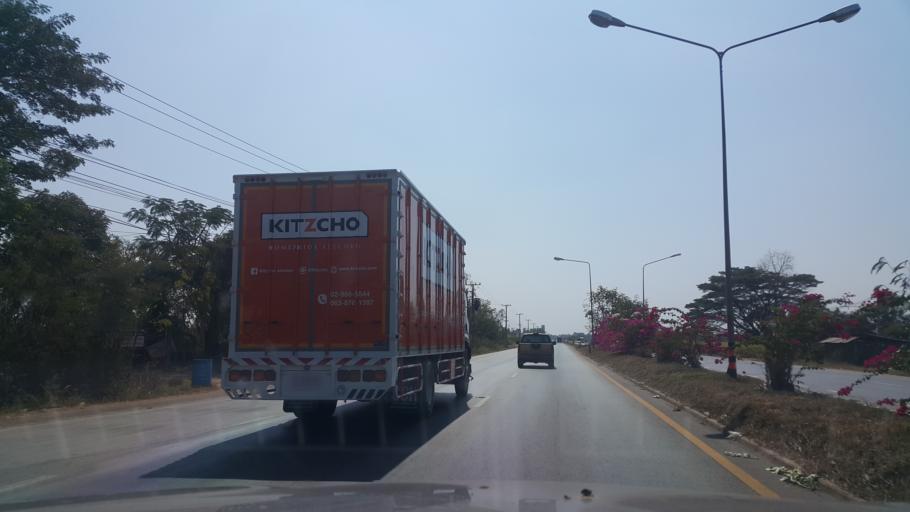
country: TH
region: Changwat Udon Thani
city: Non Sa-at
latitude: 17.0125
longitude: 102.8985
